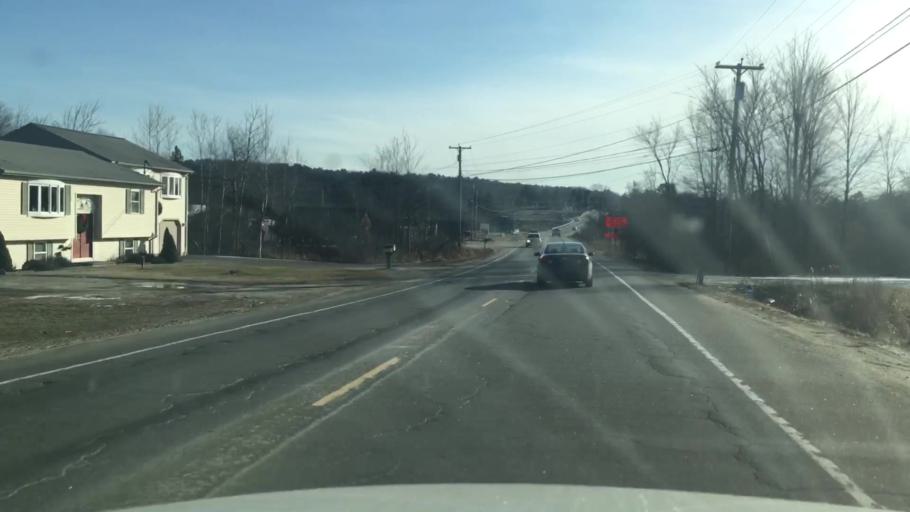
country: US
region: Maine
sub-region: Androscoggin County
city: Sabattus
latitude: 44.1061
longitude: -70.0881
